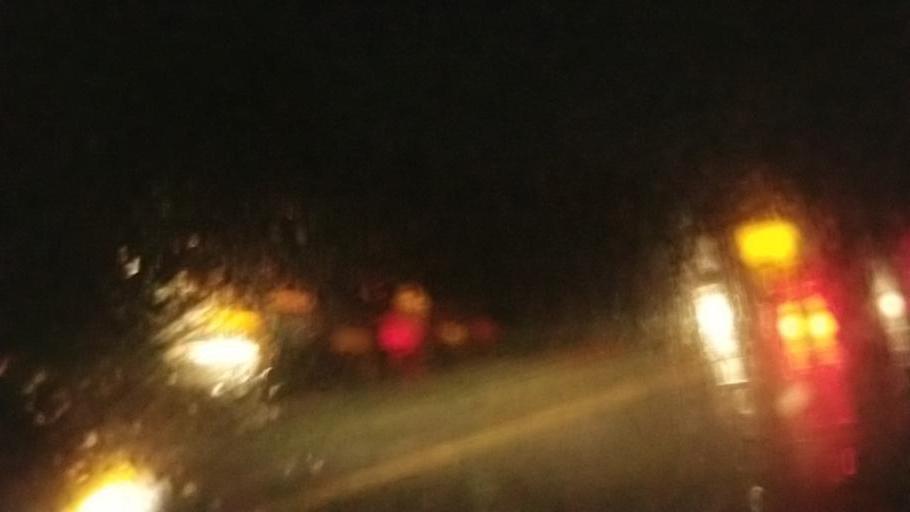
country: US
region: New York
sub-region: Seneca County
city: Seneca Falls
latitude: 42.9751
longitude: -76.8075
